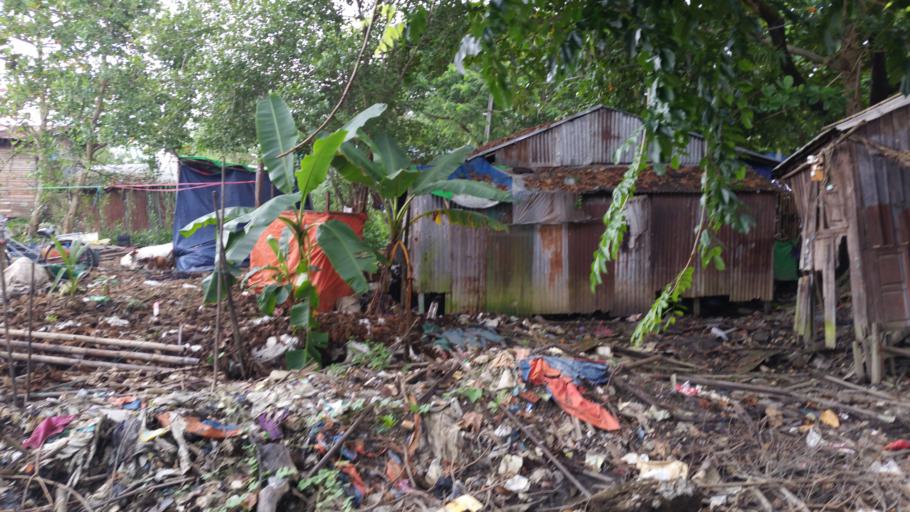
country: MM
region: Yangon
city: Yangon
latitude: 16.7651
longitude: 96.1453
